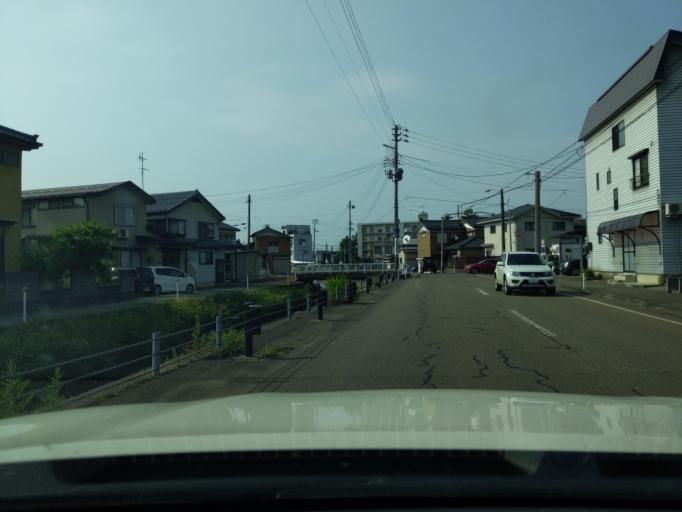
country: JP
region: Niigata
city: Nagaoka
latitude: 37.4357
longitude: 138.8566
